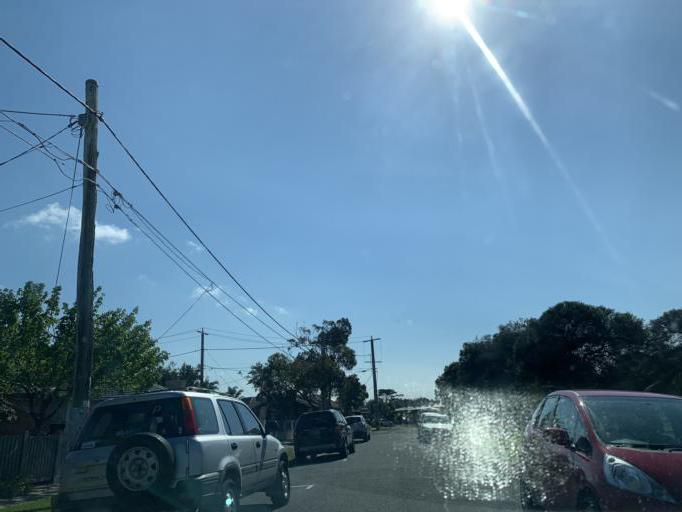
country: AU
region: Victoria
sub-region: Kingston
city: Mordialloc
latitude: -38.0124
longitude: 145.0953
